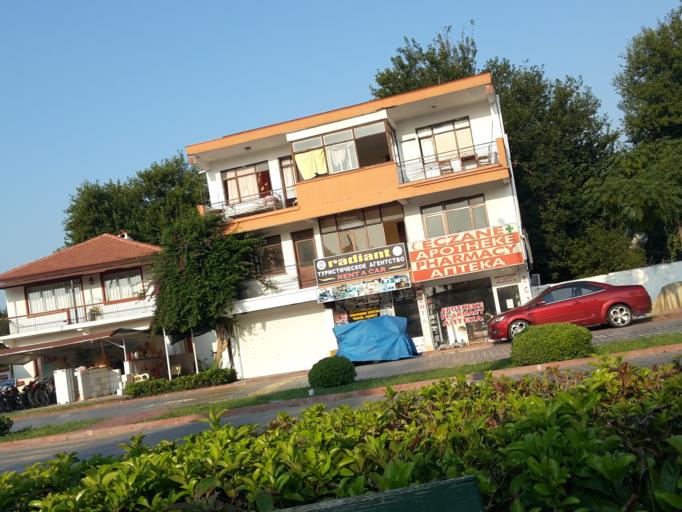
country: TR
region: Antalya
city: Kemer
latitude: 36.6047
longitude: 30.5592
